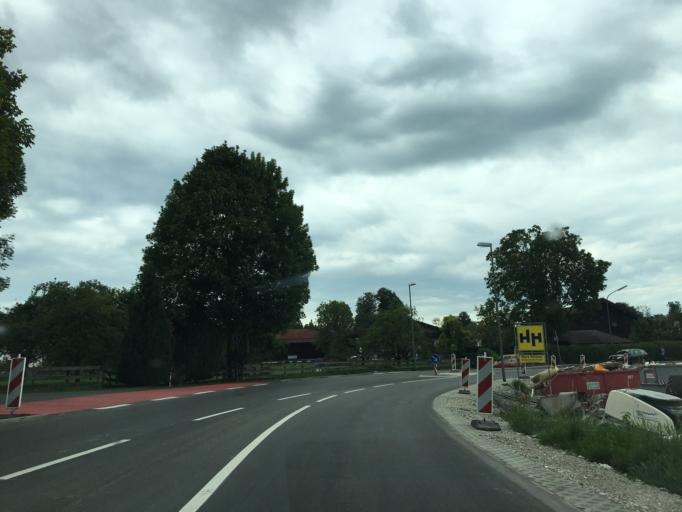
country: DE
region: Bavaria
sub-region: Upper Bavaria
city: Brannenburg
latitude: 47.7334
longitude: 12.1077
